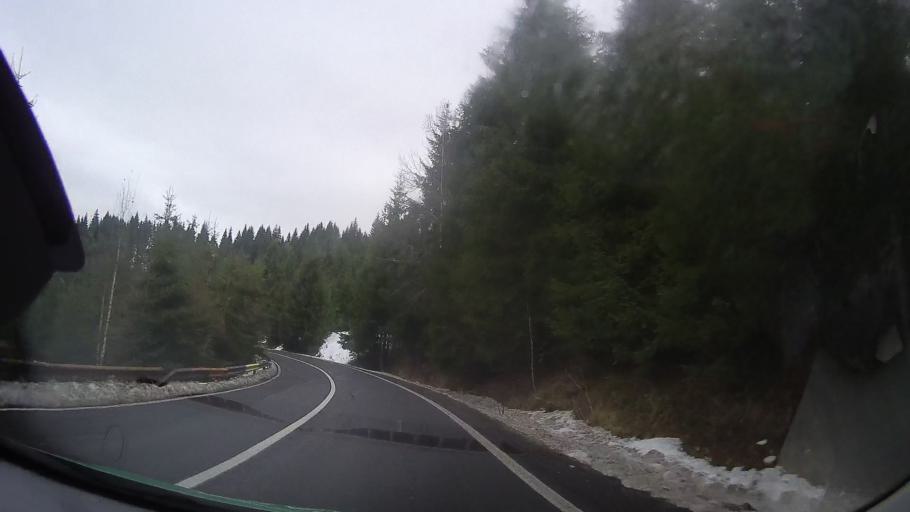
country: RO
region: Harghita
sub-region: Municipiul Gheorgheni
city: Gheorgheni
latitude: 46.7767
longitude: 25.7122
